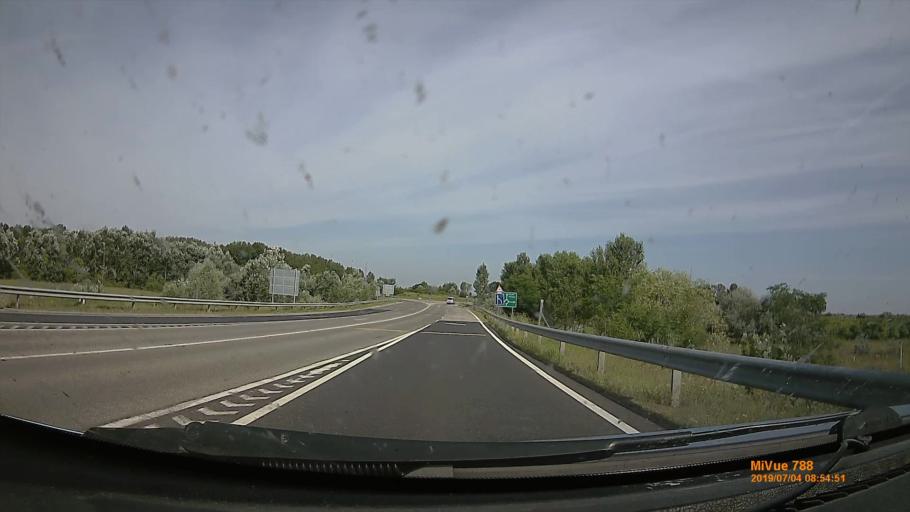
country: HU
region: Pest
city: Vecses
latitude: 47.3784
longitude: 19.2613
